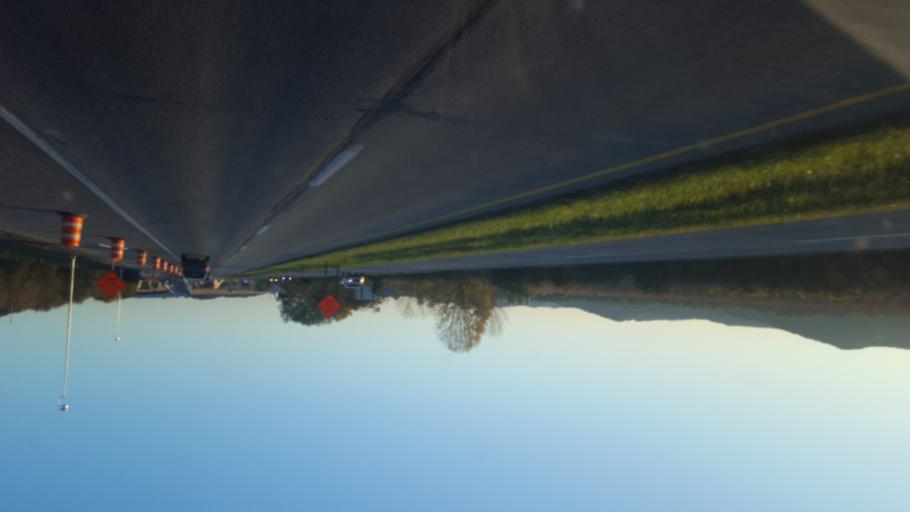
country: US
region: Ohio
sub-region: Scioto County
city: Lucasville
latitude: 38.8863
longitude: -82.9973
